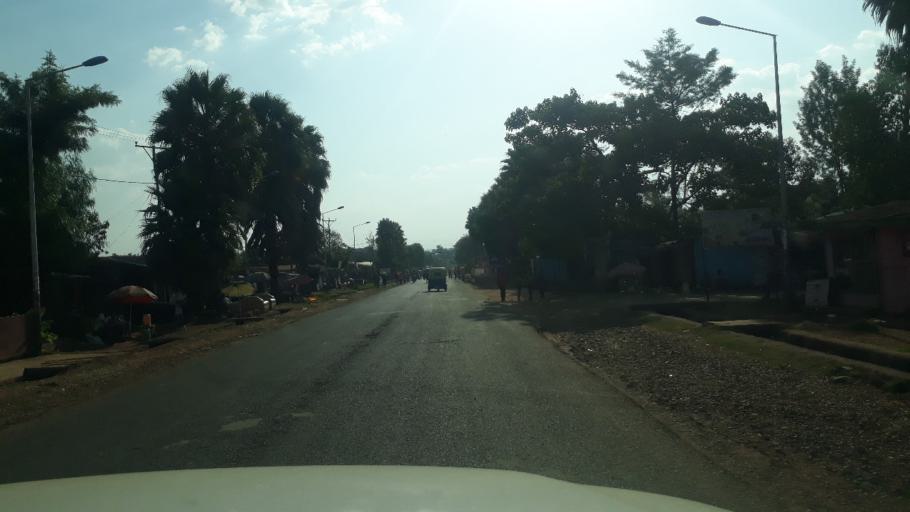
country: ET
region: Oromiya
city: Jima
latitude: 7.6837
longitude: 36.8457
